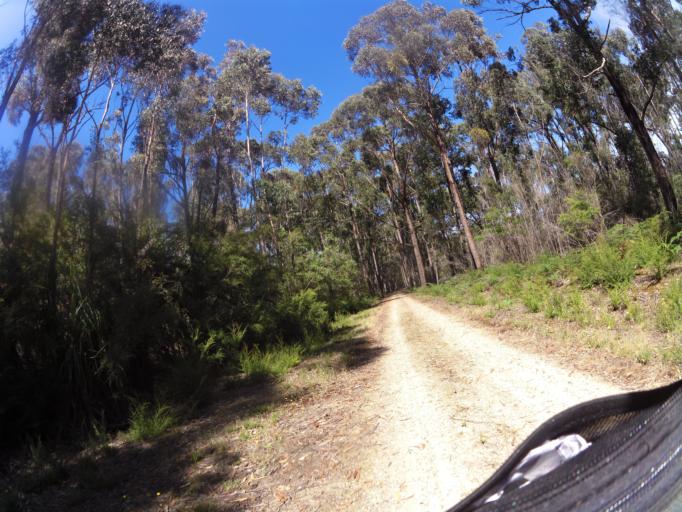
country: AU
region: Victoria
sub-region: East Gippsland
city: Lakes Entrance
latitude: -37.7185
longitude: 148.1296
